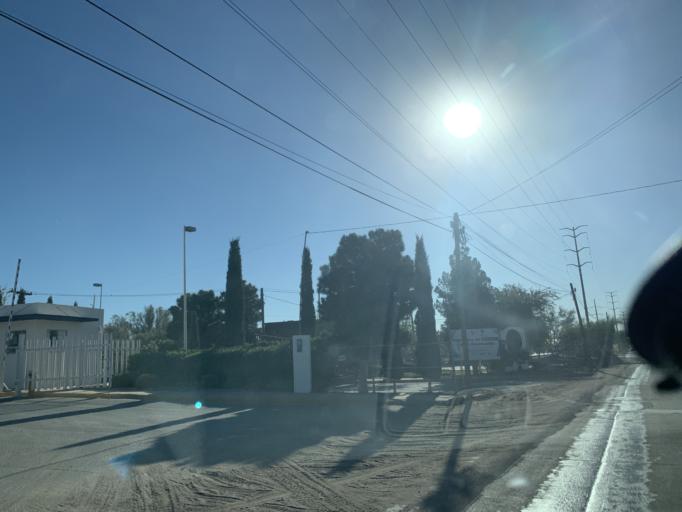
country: US
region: Texas
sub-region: El Paso County
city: Socorro
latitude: 31.7074
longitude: -106.3744
